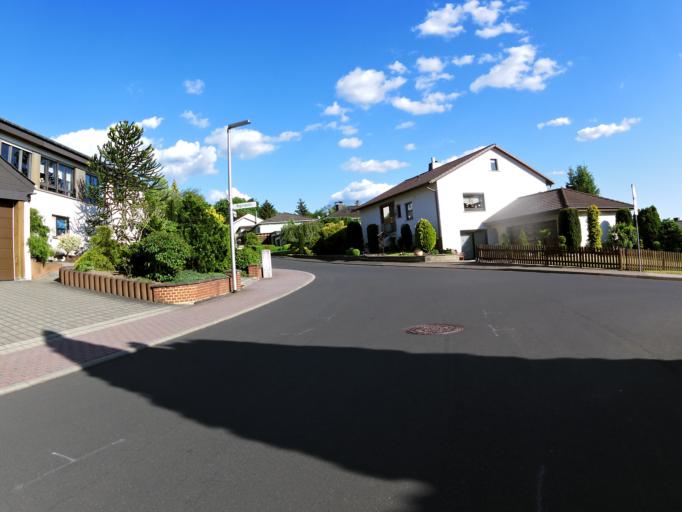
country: DE
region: Hesse
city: Philippsthal
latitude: 50.8360
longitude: 10.0162
